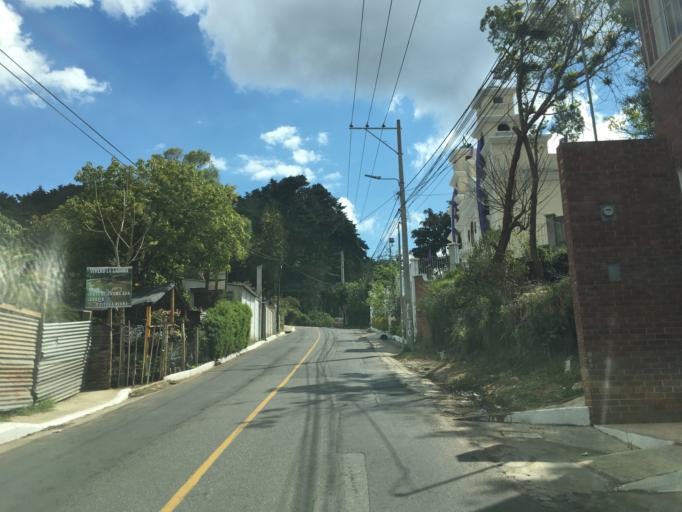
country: GT
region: Guatemala
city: San Jose Pinula
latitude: 14.5661
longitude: -90.4397
